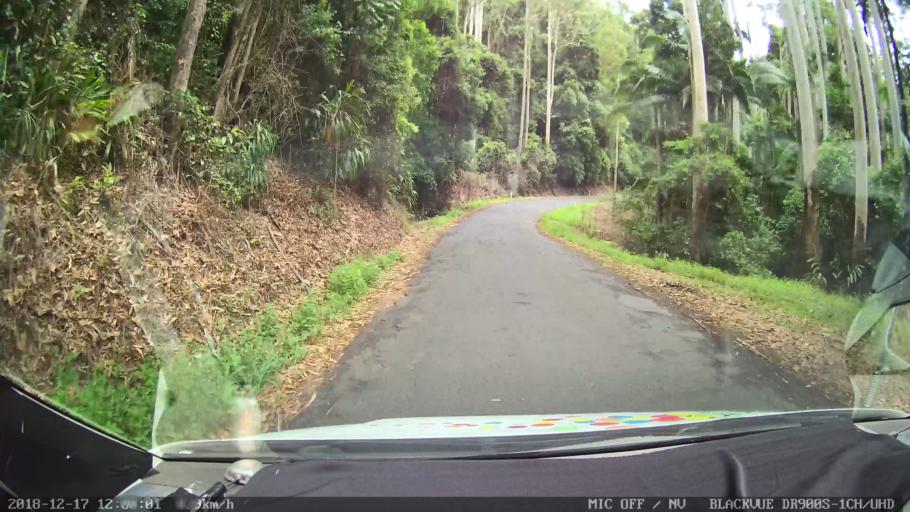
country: AU
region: New South Wales
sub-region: Kyogle
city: Kyogle
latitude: -28.5276
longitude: 152.5667
